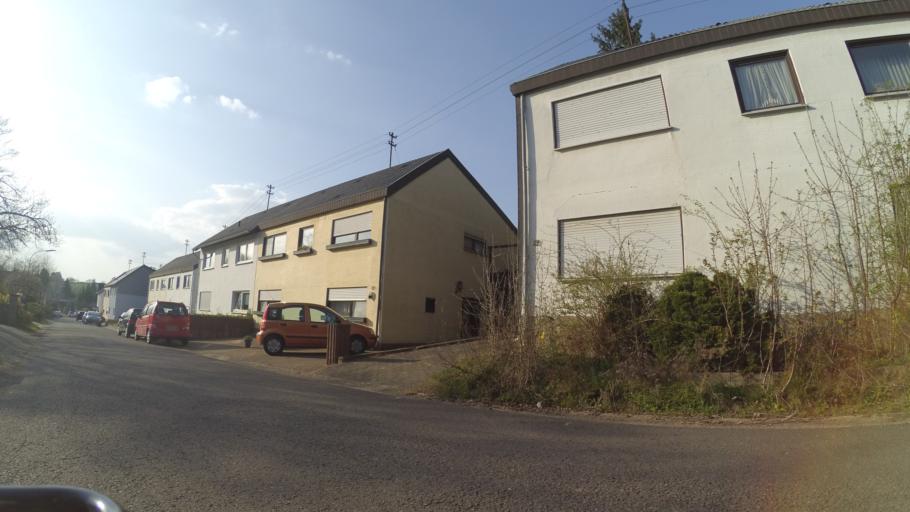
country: DE
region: Saarland
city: Heusweiler
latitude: 49.3452
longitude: 6.9403
